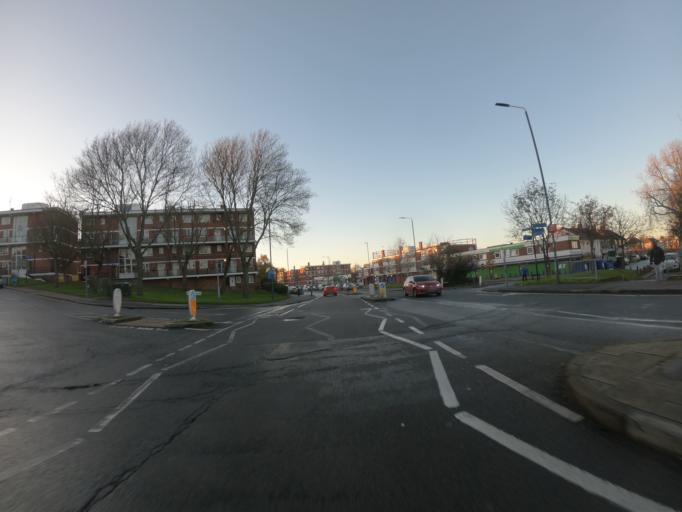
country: GB
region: England
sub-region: Greater London
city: Belvedere
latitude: 51.4908
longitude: 0.1518
